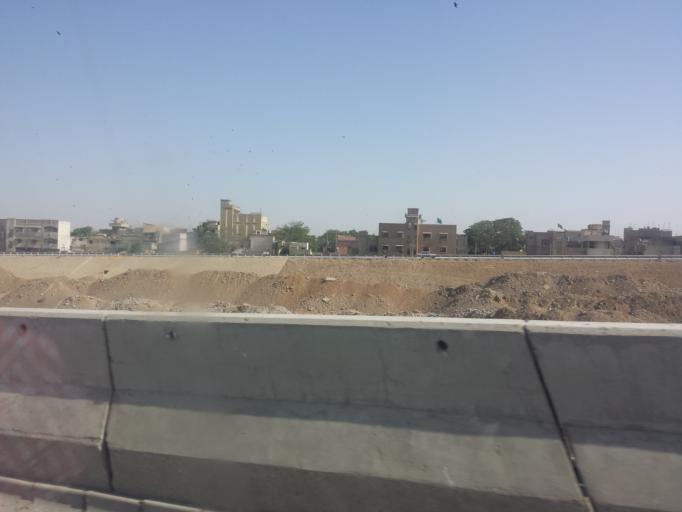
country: PK
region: Sindh
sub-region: Karachi District
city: Karachi
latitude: 24.8927
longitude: 67.0414
